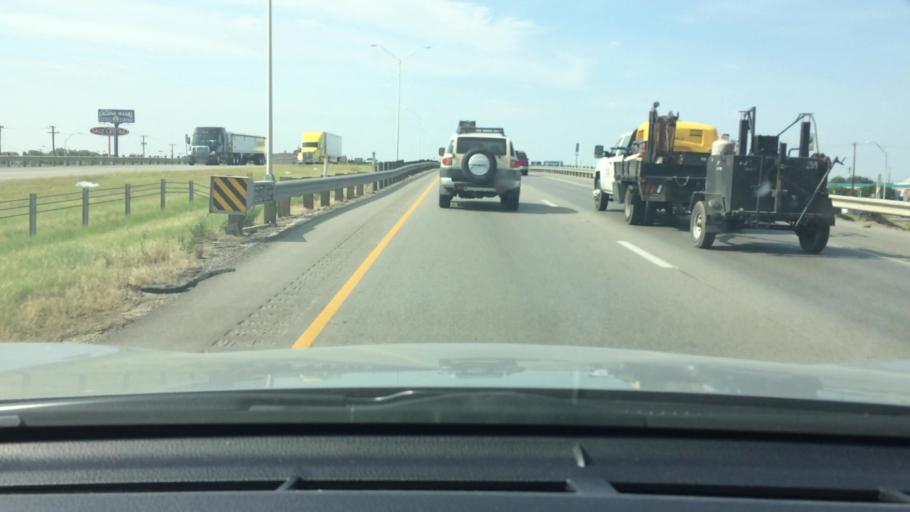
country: US
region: Texas
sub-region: Bexar County
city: China Grove
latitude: 29.3968
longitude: -98.3892
